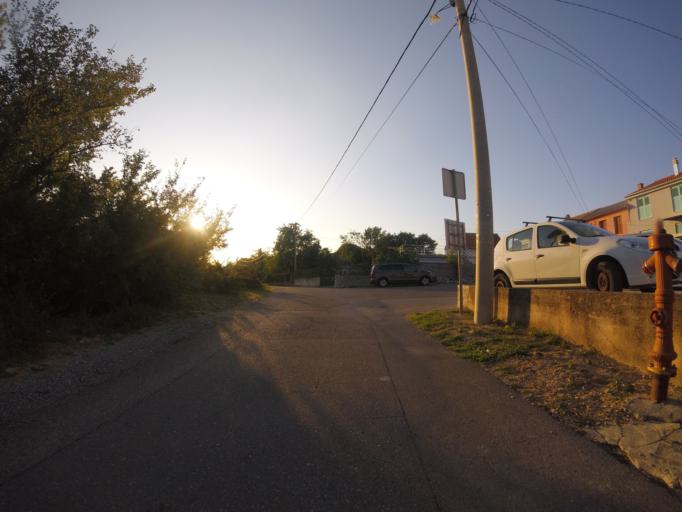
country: HR
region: Primorsko-Goranska
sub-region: Grad Crikvenica
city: Jadranovo
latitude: 45.2157
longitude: 14.6298
